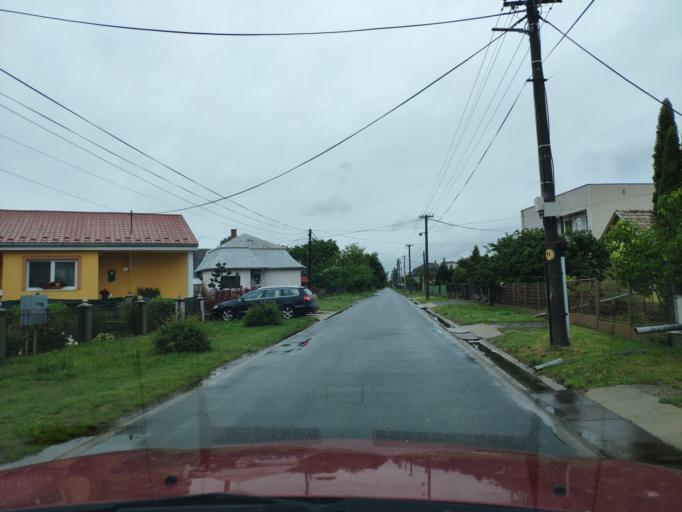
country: SK
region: Kosicky
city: Cierna nad Tisou
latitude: 48.4112
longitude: 22.0616
